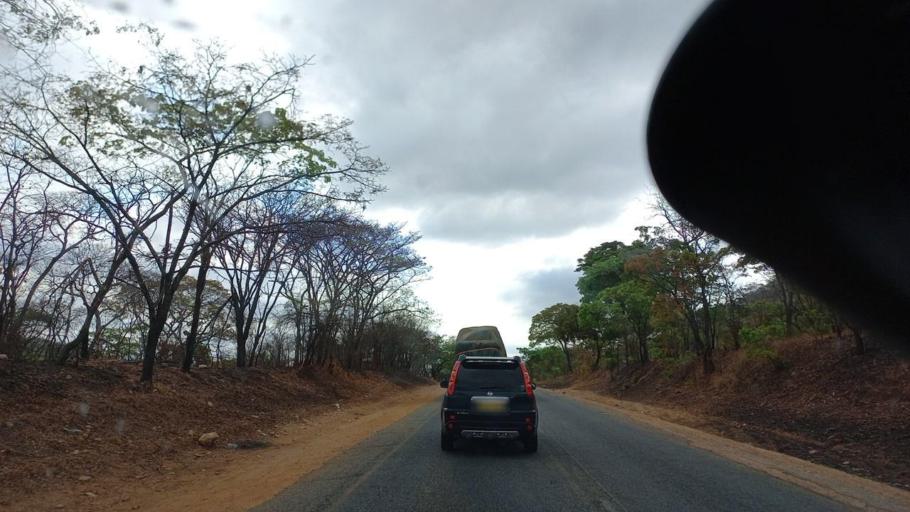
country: ZM
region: Lusaka
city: Chongwe
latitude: -15.1497
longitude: 29.3635
